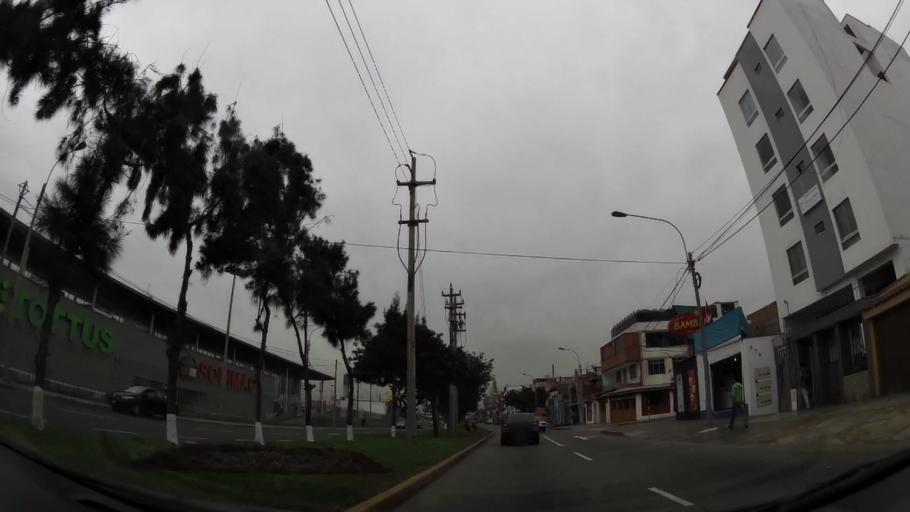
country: PE
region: Callao
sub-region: Callao
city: Callao
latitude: -12.0807
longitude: -77.0882
